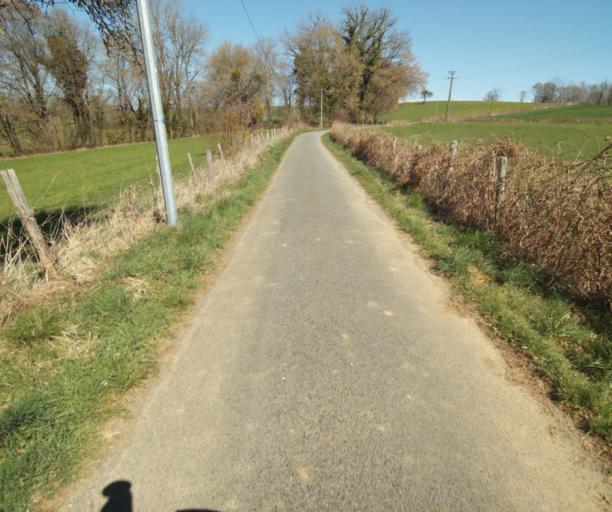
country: FR
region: Limousin
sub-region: Departement de la Correze
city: Chamboulive
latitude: 45.4298
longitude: 1.6806
